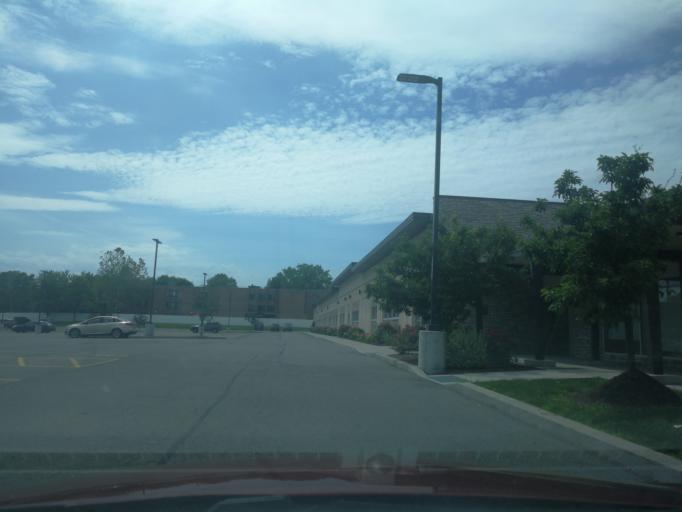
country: US
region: New York
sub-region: Monroe County
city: Irondequoit
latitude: 43.1906
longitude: -77.5846
